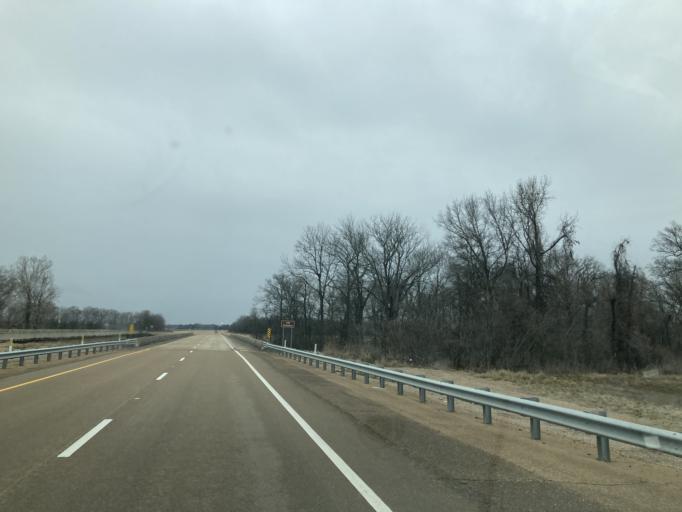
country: US
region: Mississippi
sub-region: Humphreys County
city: Belzoni
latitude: 33.0756
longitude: -90.4772
